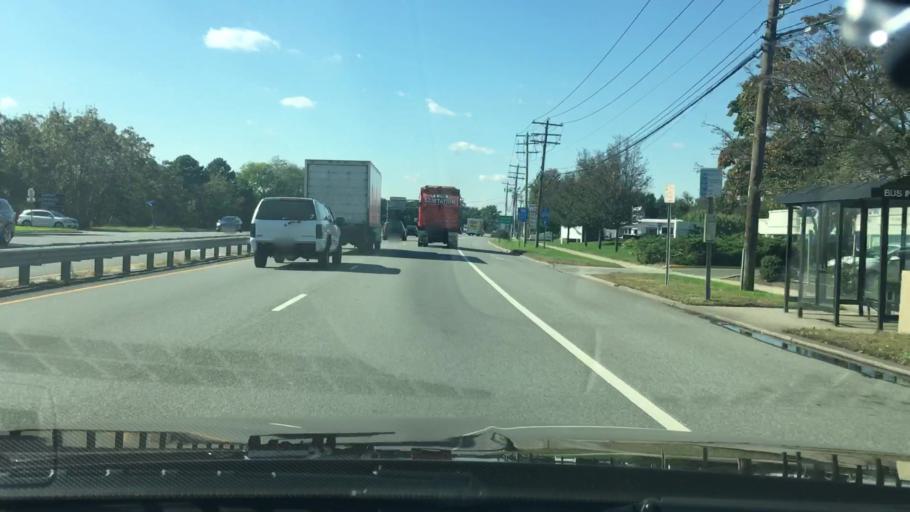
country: US
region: New York
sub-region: Suffolk County
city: Bohemia
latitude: 40.7827
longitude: -73.0987
